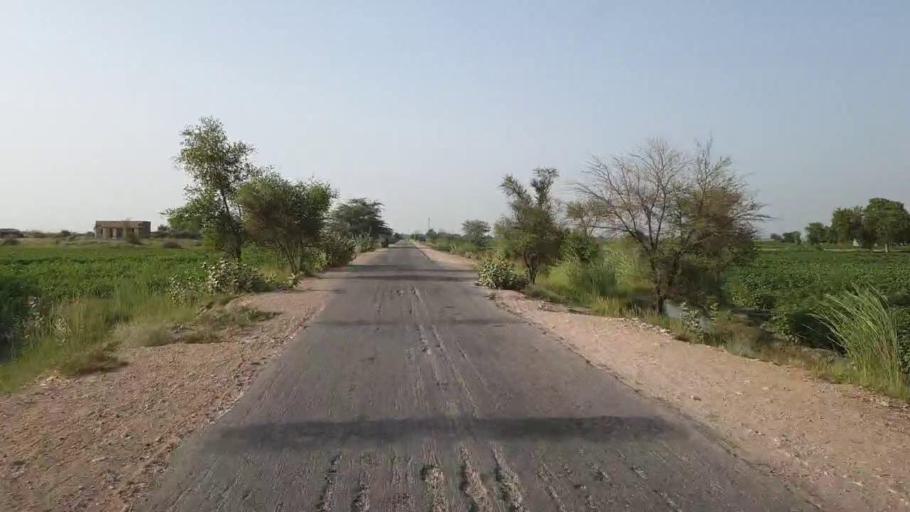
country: PK
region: Sindh
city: Jam Sahib
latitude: 26.4689
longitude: 68.8592
